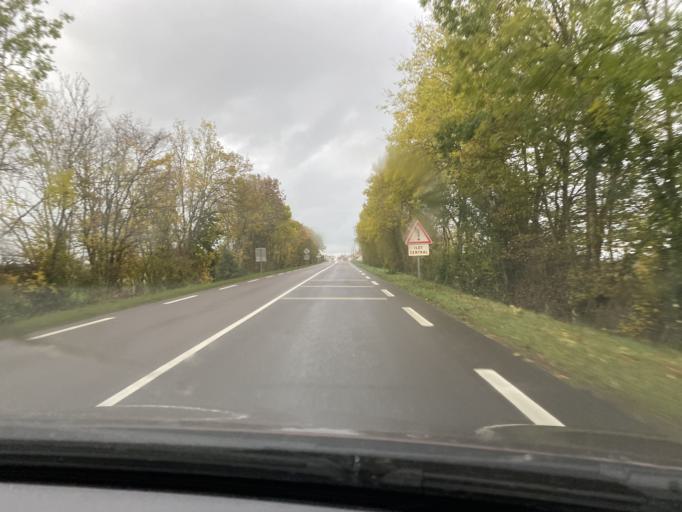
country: FR
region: Bourgogne
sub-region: Departement de la Cote-d'Or
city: Saulieu
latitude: 47.3387
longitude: 4.1953
